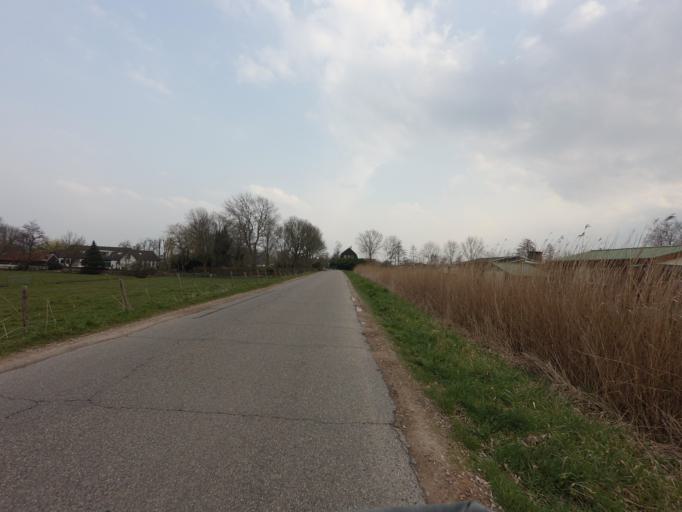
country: NL
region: Utrecht
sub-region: Gemeente De Ronde Venen
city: Mijdrecht
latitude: 52.1857
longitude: 4.8405
